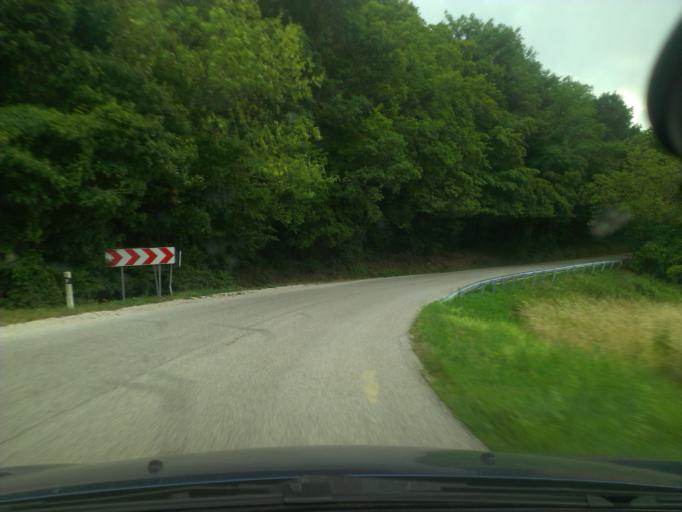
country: SK
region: Trnavsky
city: Vrbove
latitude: 48.6764
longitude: 17.6940
